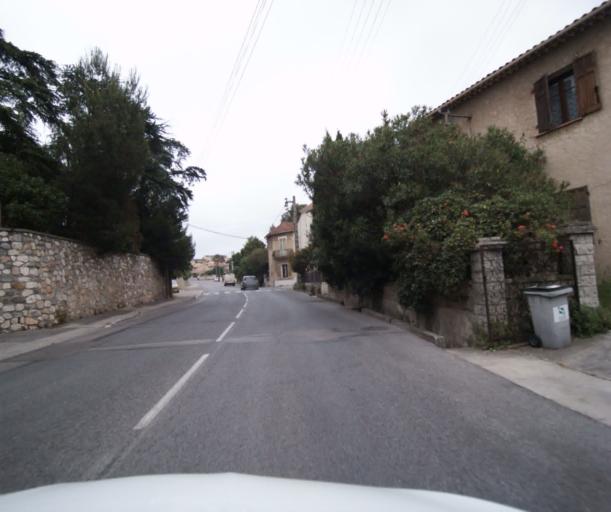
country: FR
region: Provence-Alpes-Cote d'Azur
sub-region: Departement du Var
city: La Seyne-sur-Mer
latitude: 43.0935
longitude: 5.8894
